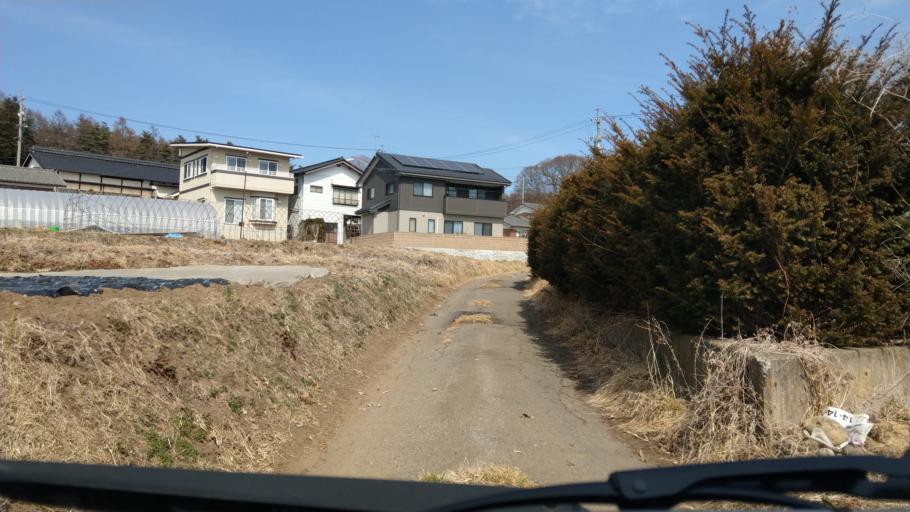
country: JP
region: Nagano
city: Komoro
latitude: 36.3334
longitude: 138.4627
